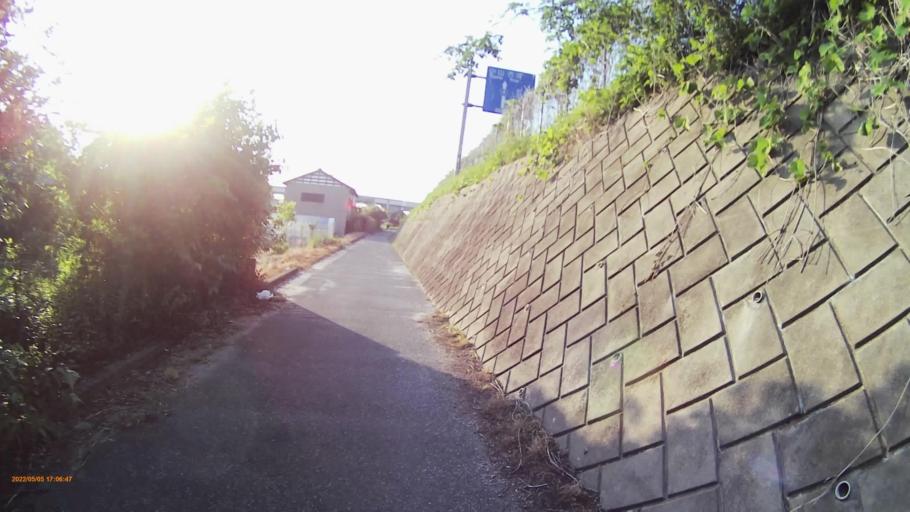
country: JP
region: Saitama
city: Kurihashi
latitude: 36.1219
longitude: 139.7159
